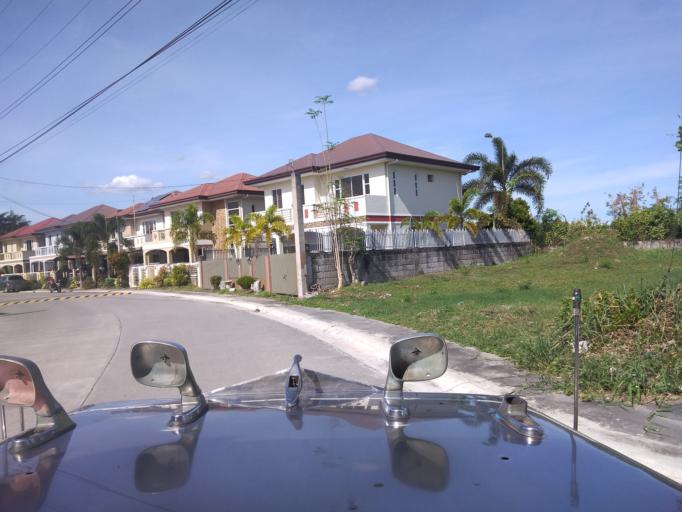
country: PH
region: Central Luzon
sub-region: Province of Pampanga
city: Magliman
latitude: 15.0203
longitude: 120.6579
